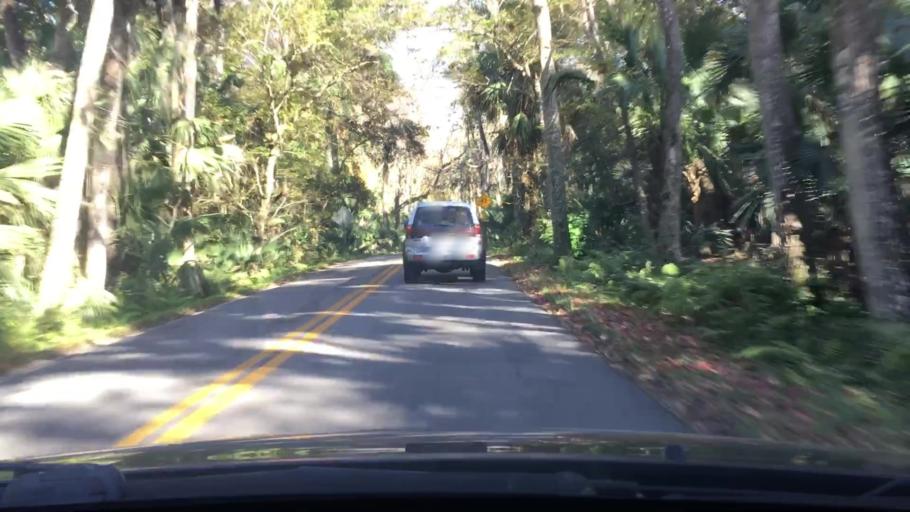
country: US
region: Florida
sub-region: Flagler County
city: Flagler Beach
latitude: 29.4035
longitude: -81.1368
